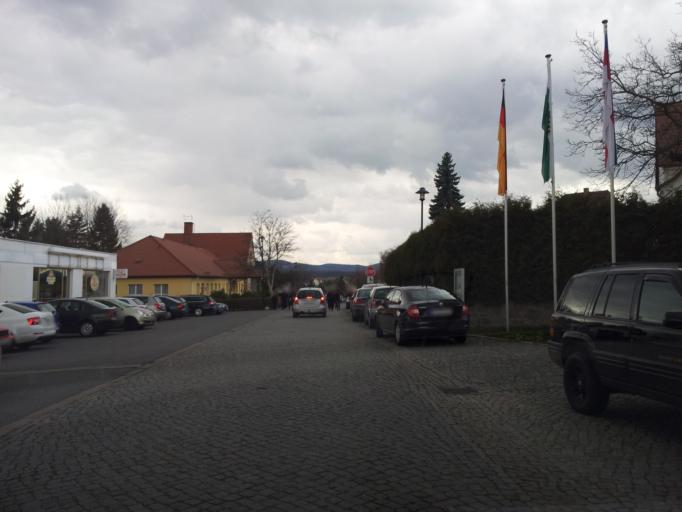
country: DE
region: Saxony
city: Panschwitz-Kuckau
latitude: 51.2334
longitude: 14.1948
